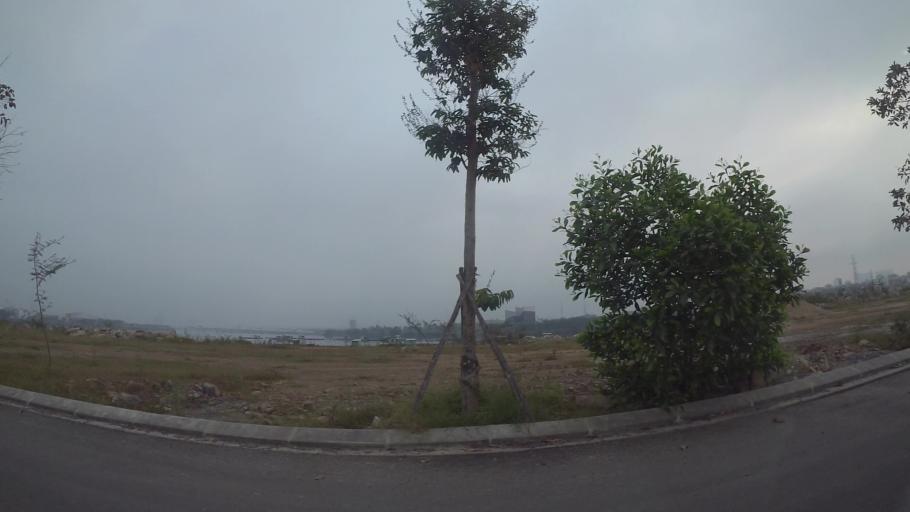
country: VN
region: Da Nang
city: Ngu Hanh Son
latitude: 16.0248
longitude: 108.2347
